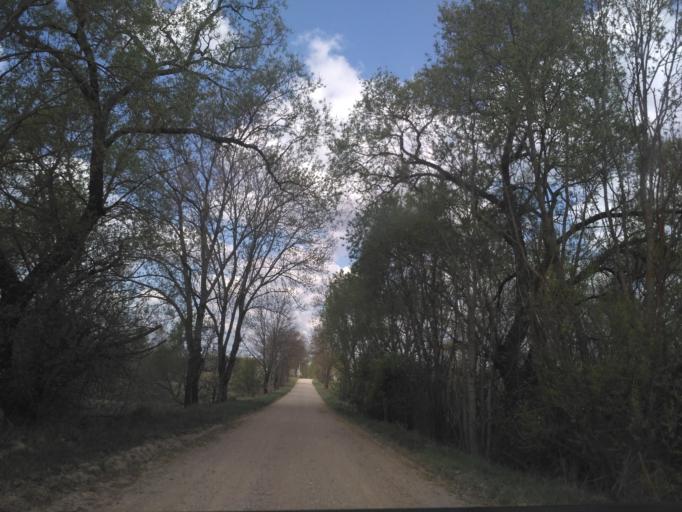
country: BY
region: Minsk
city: Il'ya
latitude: 54.2802
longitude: 27.3032
